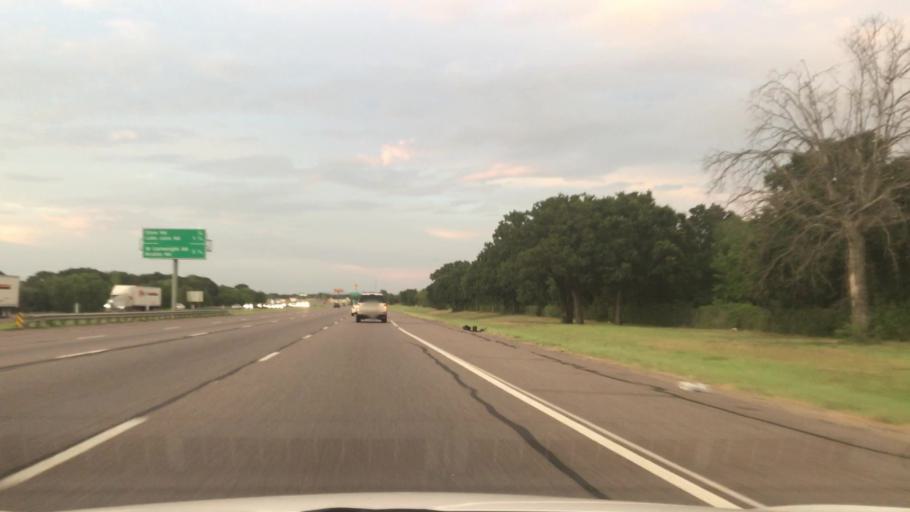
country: US
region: Texas
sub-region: Dallas County
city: Balch Springs
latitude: 32.7116
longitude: -96.6199
